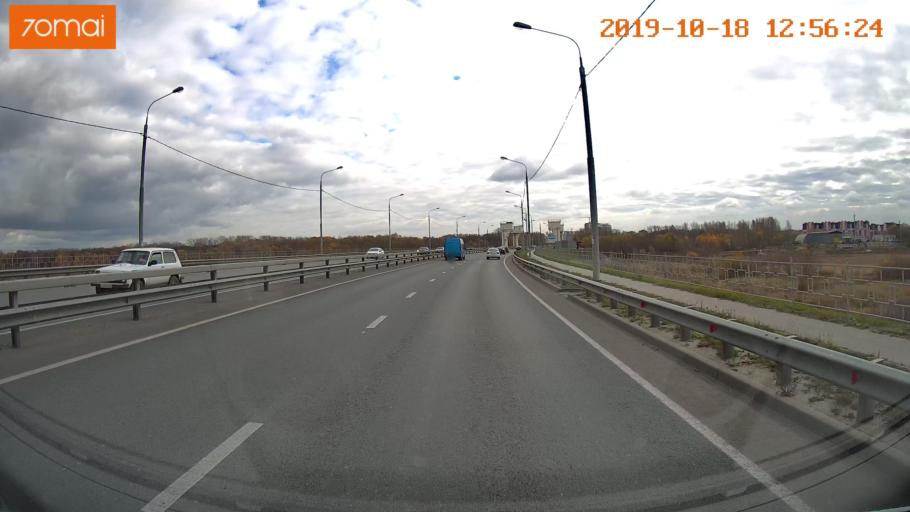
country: RU
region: Rjazan
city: Ryazan'
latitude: 54.6462
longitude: 39.7576
